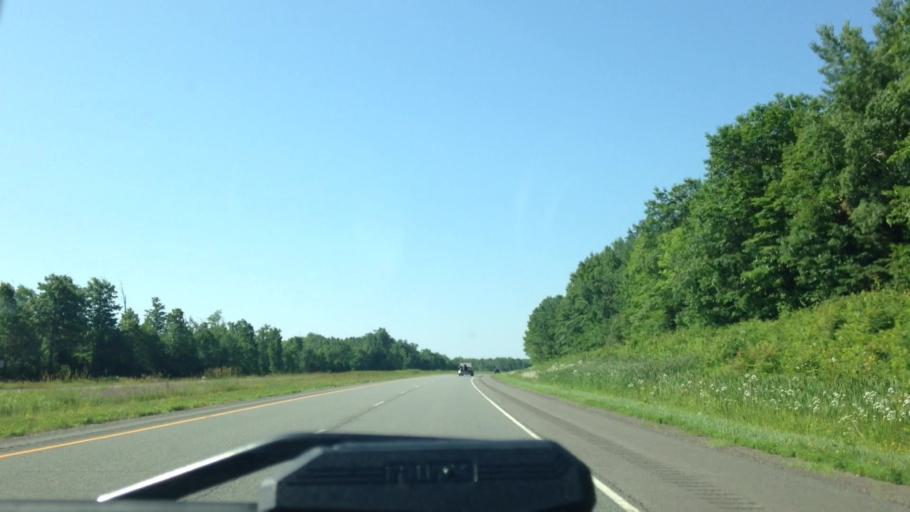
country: US
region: Wisconsin
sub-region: Douglas County
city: Lake Nebagamon
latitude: 46.4155
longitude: -91.8104
